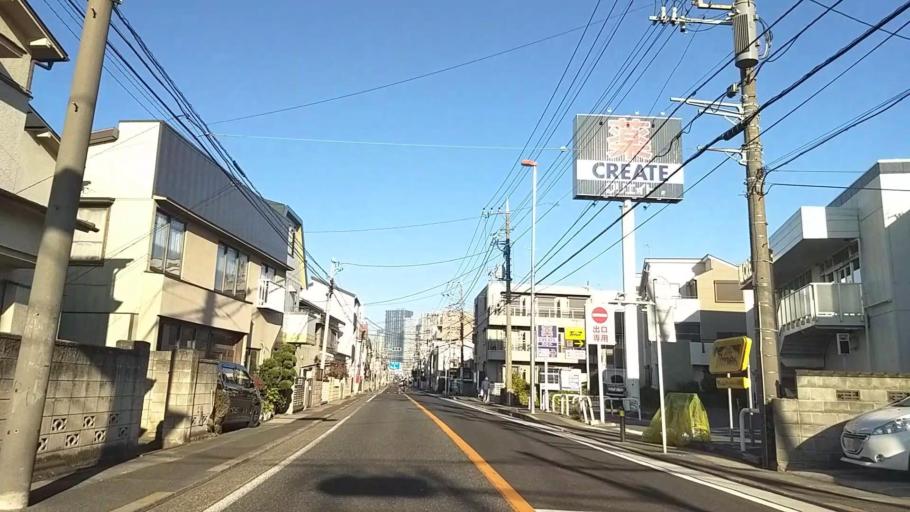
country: JP
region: Kanagawa
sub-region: Kawasaki-shi
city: Kawasaki
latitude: 35.5590
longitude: 139.6712
